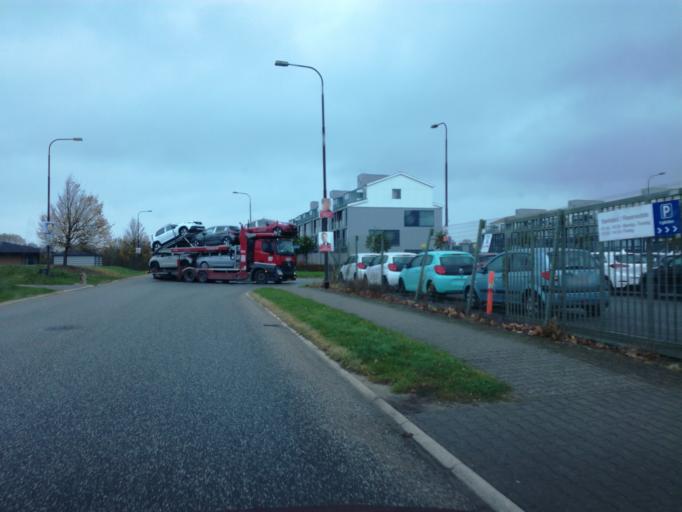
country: DK
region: South Denmark
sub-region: Fredericia Kommune
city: Fredericia
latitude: 55.5701
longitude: 9.7126
